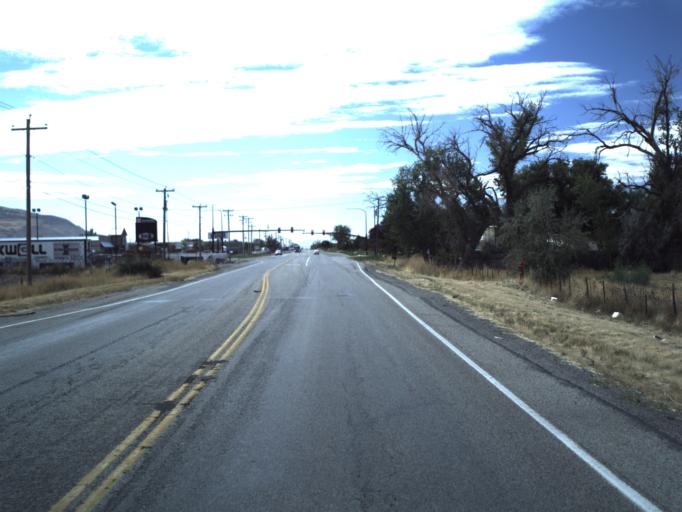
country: US
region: Utah
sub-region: Davis County
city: West Bountiful
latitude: 40.8768
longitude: -111.9301
